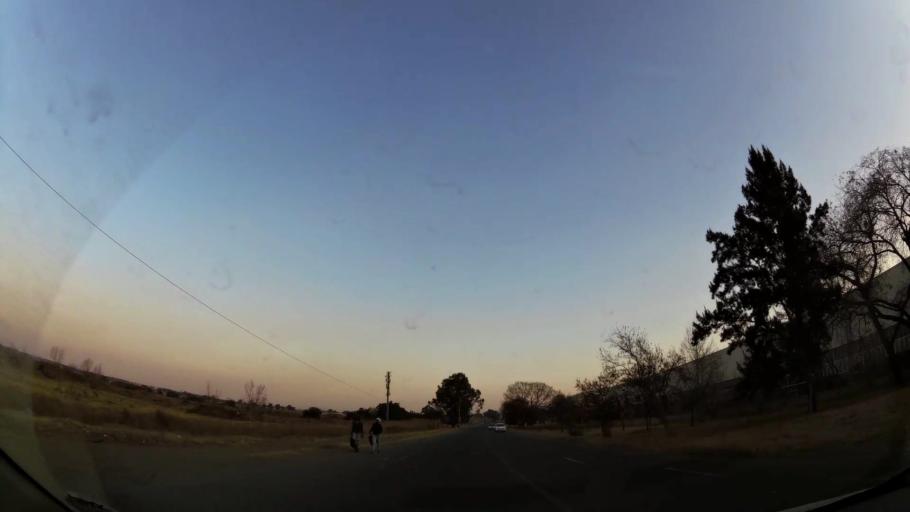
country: ZA
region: Gauteng
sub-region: Ekurhuleni Metropolitan Municipality
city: Springs
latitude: -26.2725
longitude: 28.4063
